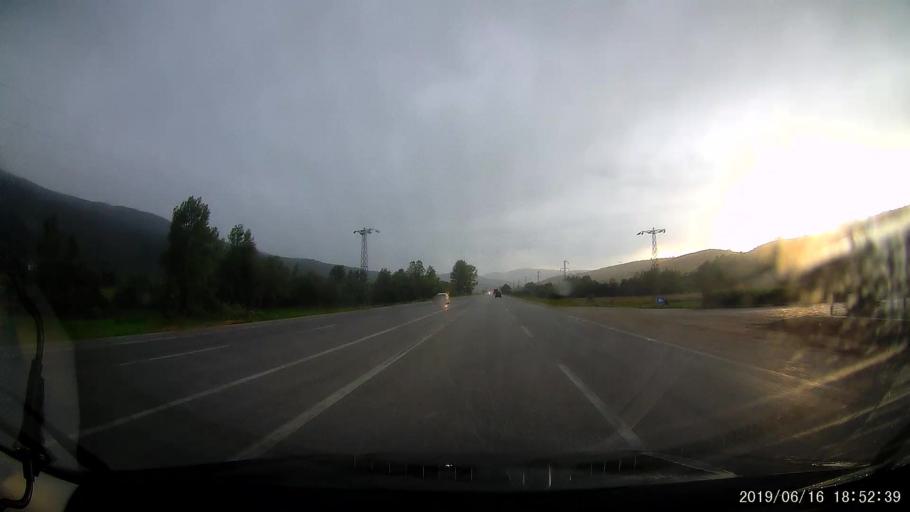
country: TR
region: Erzincan
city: Catalcam
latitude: 39.9017
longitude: 38.8964
